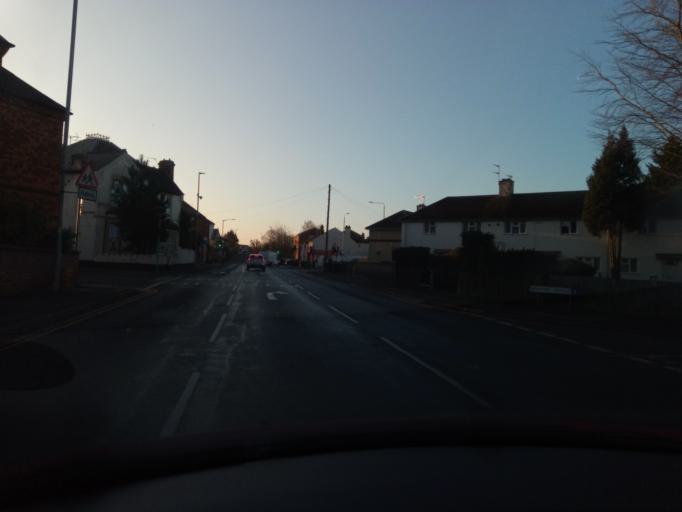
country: GB
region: England
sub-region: Leicestershire
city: Loughborough
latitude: 52.7804
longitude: -1.2017
